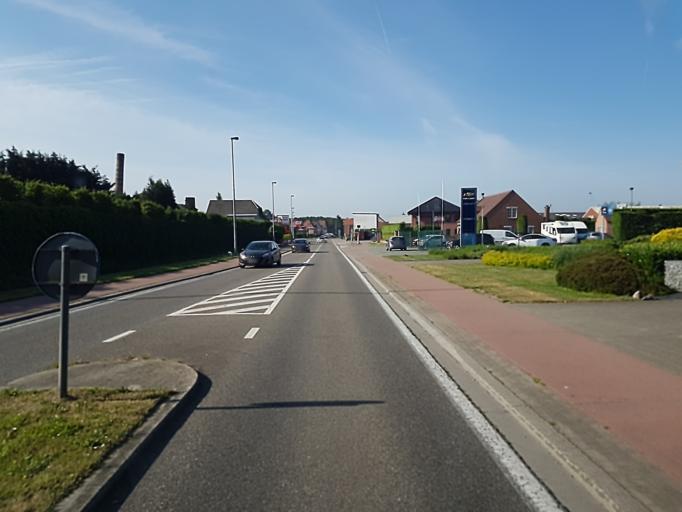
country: BE
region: Flanders
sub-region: Provincie Oost-Vlaanderen
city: Beveren
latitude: 51.2143
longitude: 4.1959
